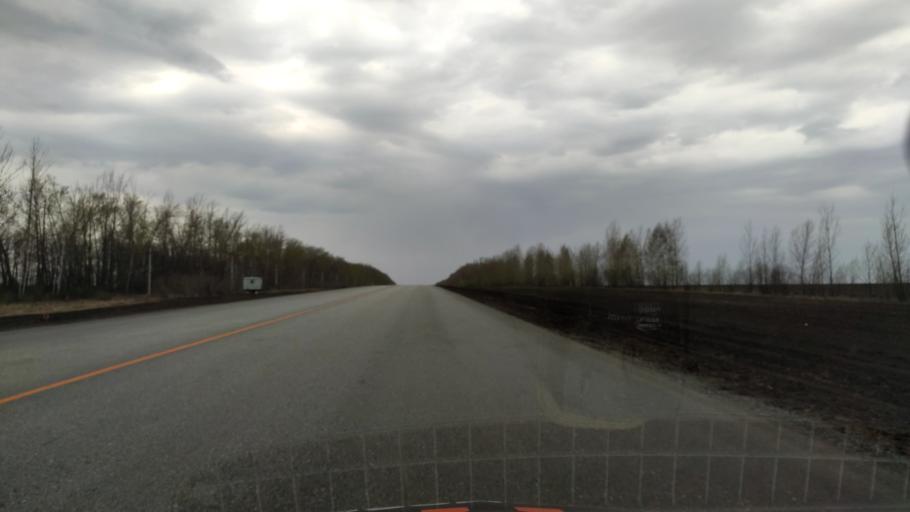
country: RU
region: Kursk
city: Gorshechnoye
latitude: 51.5482
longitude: 38.0980
